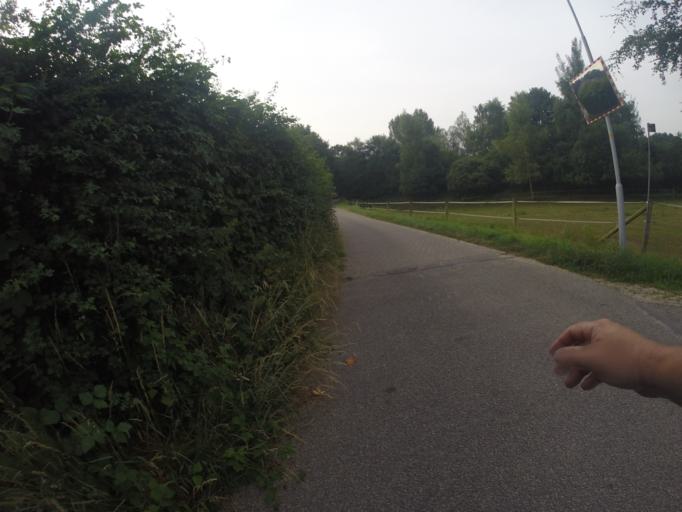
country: NL
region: Gelderland
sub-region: Gemeente Zevenaar
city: Zevenaar
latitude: 51.9037
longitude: 6.1371
